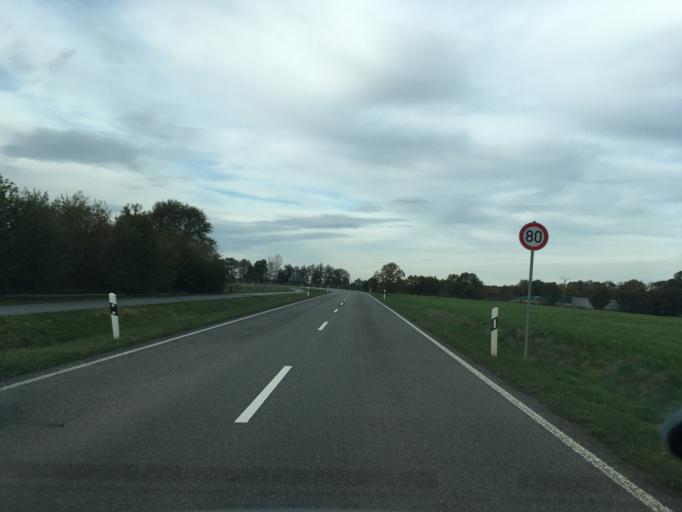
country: DE
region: North Rhine-Westphalia
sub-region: Regierungsbezirk Munster
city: Velen
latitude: 51.8938
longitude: 6.9283
